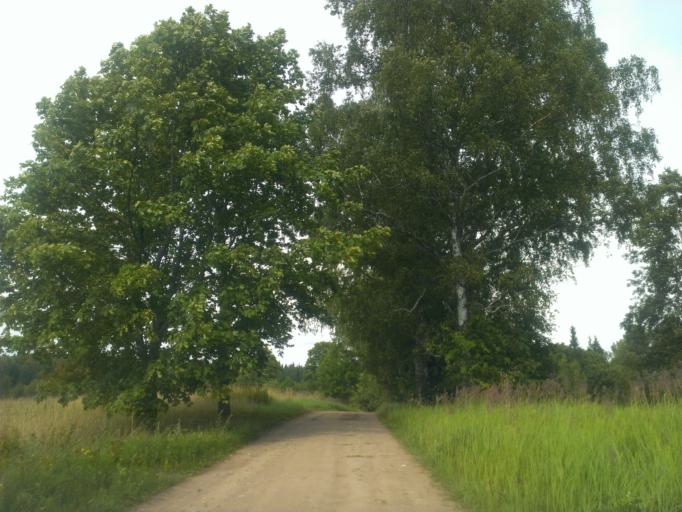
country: LV
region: Ligatne
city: Ligatne
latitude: 57.2272
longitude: 25.0109
